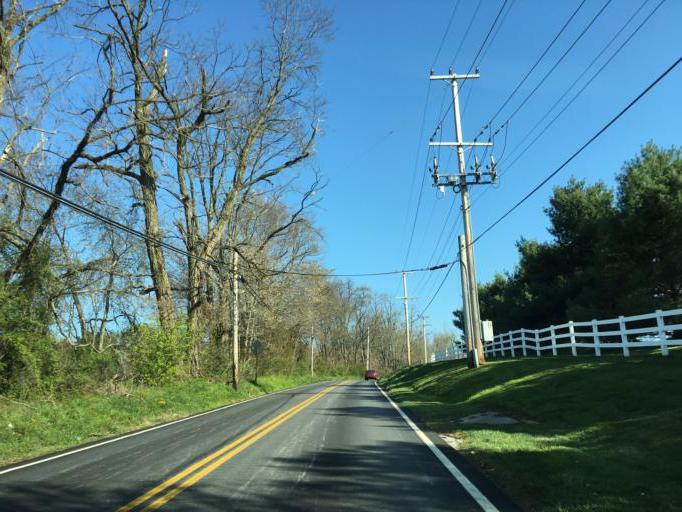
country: US
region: Maryland
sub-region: Baltimore County
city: Hampton
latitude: 39.4988
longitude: -76.5279
